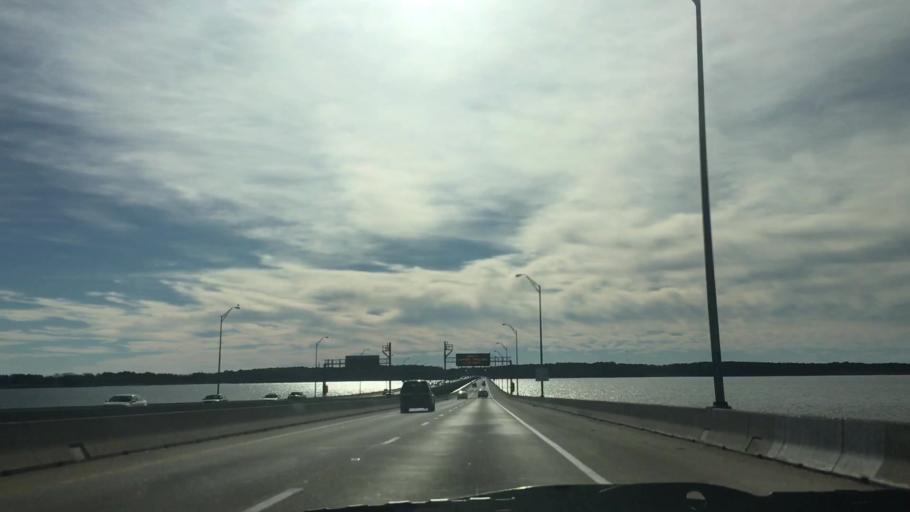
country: US
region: Virginia
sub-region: City of Newport News
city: Newport News
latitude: 36.9100
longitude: -76.4065
